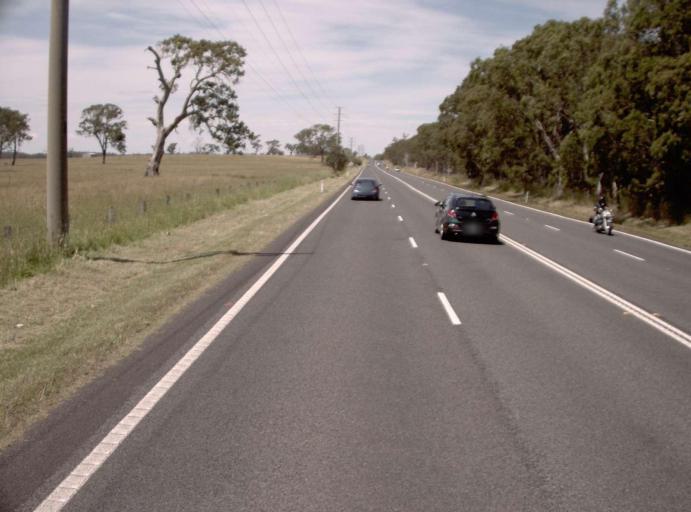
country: AU
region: Victoria
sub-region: Latrobe
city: Traralgon
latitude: -38.1778
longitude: 146.6354
